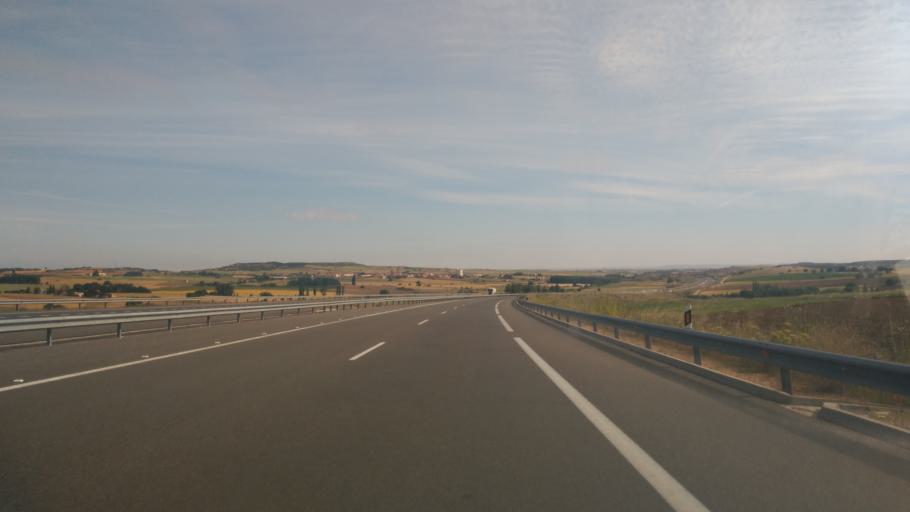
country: ES
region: Castille and Leon
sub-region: Provincia de Zamora
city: Corrales
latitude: 41.3310
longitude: -5.7265
